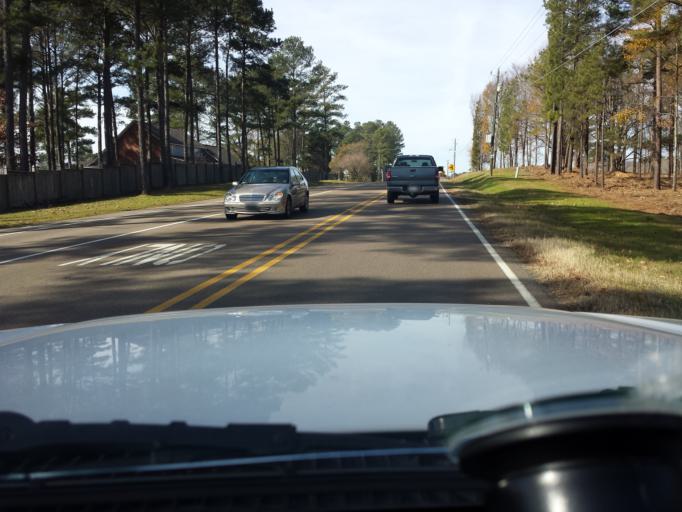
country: US
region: Mississippi
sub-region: Madison County
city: Madison
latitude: 32.4062
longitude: -90.0086
